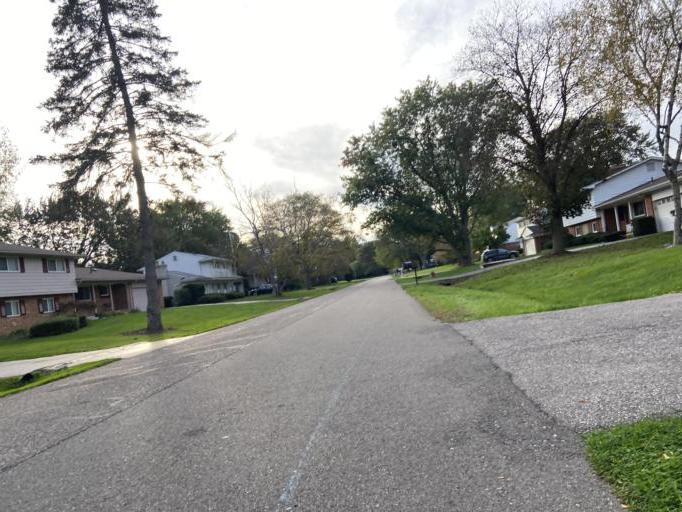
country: US
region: Michigan
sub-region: Oakland County
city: Farmington Hills
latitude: 42.5075
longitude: -83.3706
